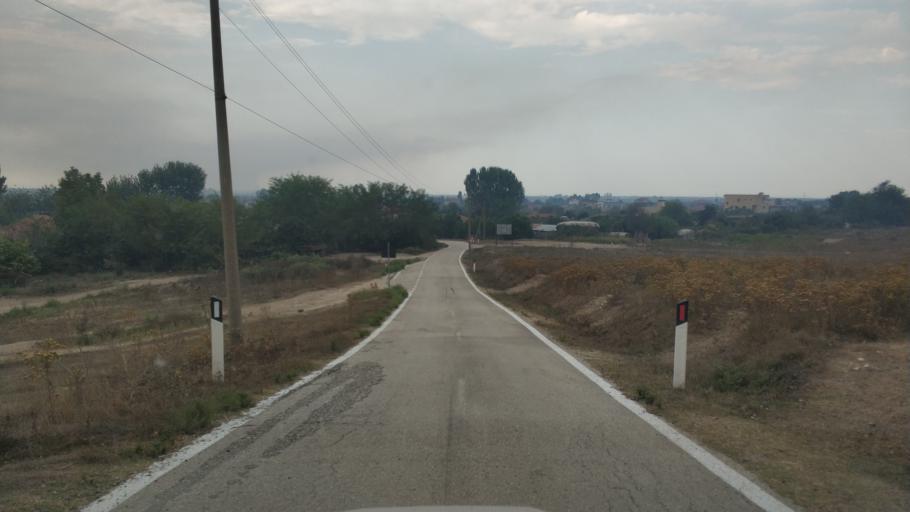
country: AL
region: Fier
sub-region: Rrethi i Fierit
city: Dermenas
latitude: 40.7249
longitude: 19.4687
